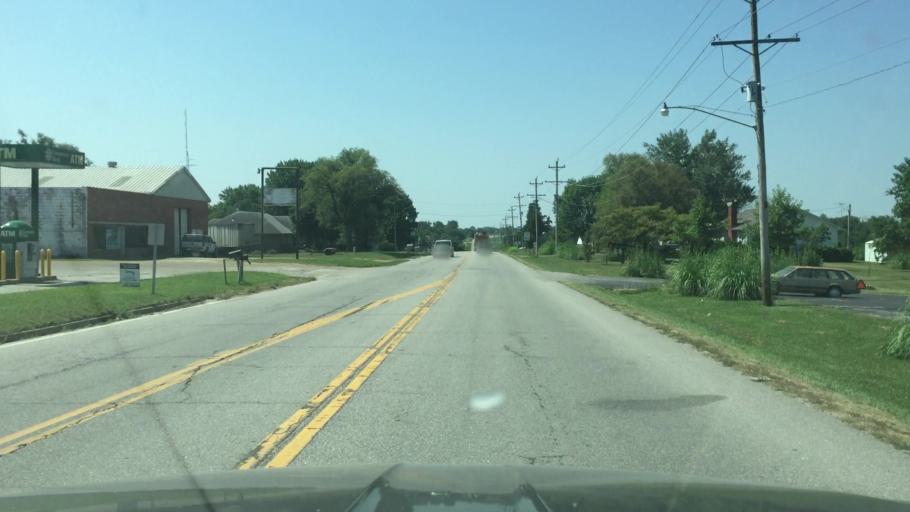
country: US
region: Missouri
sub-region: Moniteau County
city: Tipton
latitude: 38.6510
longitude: -92.7840
